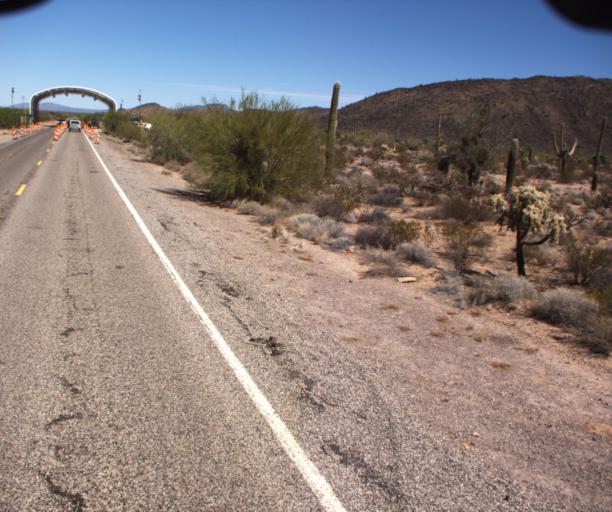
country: US
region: Arizona
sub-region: Pima County
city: Ajo
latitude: 32.2011
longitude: -112.7593
